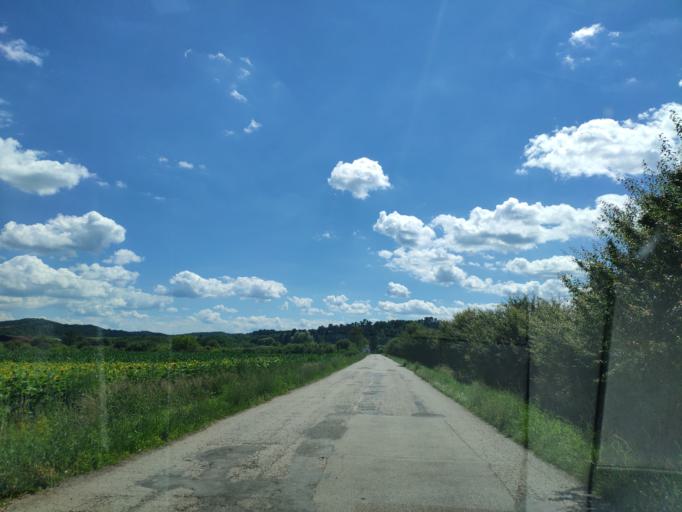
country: HU
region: Borsod-Abauj-Zemplen
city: Arlo
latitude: 48.2851
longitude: 20.1926
